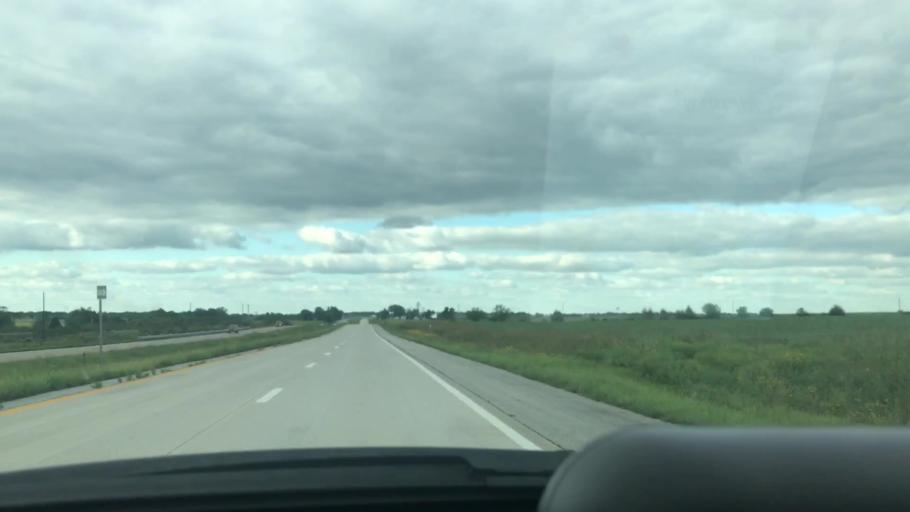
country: US
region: Missouri
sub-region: Benton County
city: Lincoln
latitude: 38.3584
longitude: -93.3392
